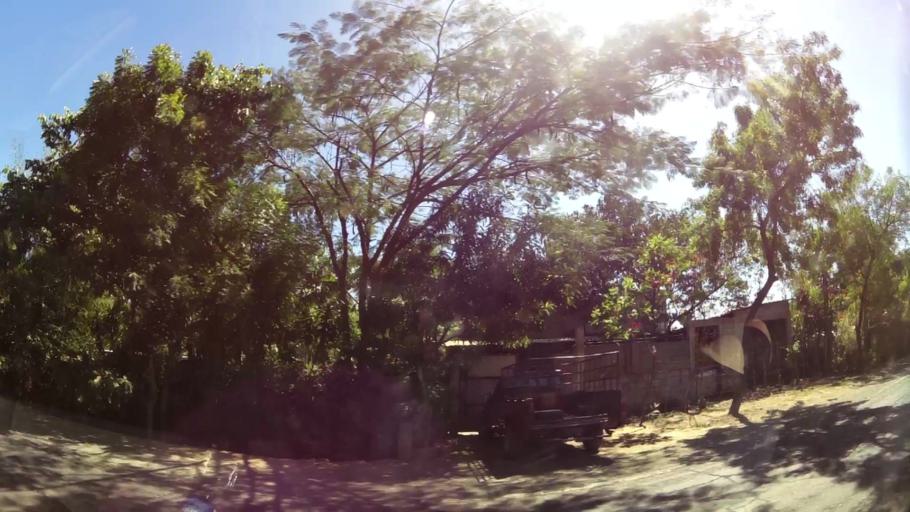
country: SV
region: Ahuachapan
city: Ahuachapan
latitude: 13.9399
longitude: -89.8445
